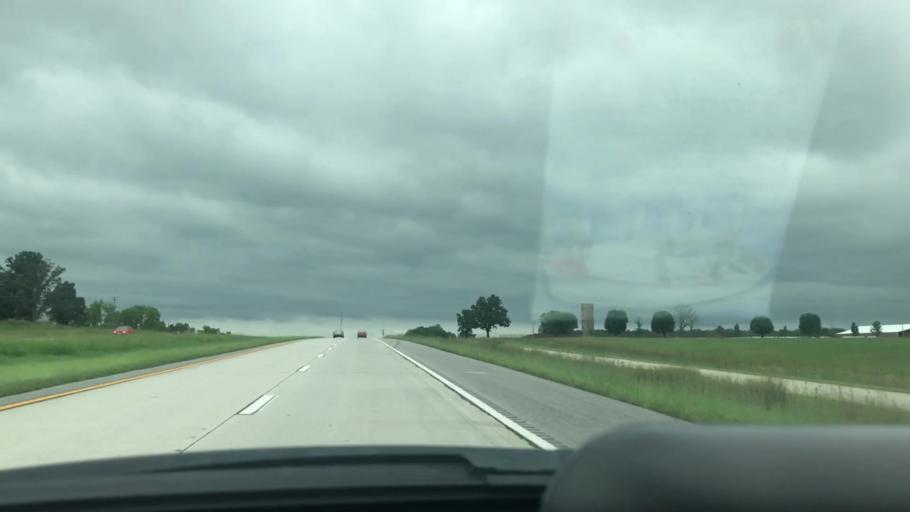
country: US
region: Missouri
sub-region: Greene County
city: Fair Grove
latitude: 37.4352
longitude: -93.1445
